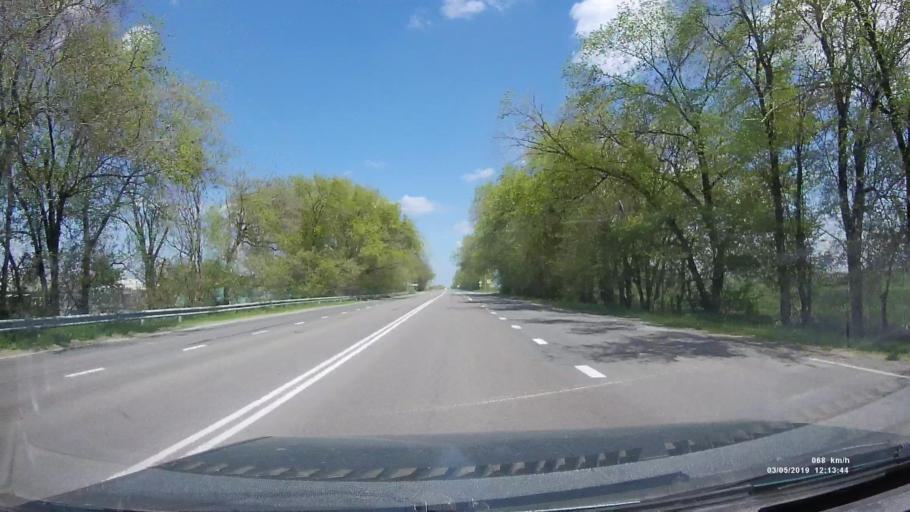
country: RU
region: Rostov
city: Melikhovskaya
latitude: 47.3355
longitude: 40.5571
